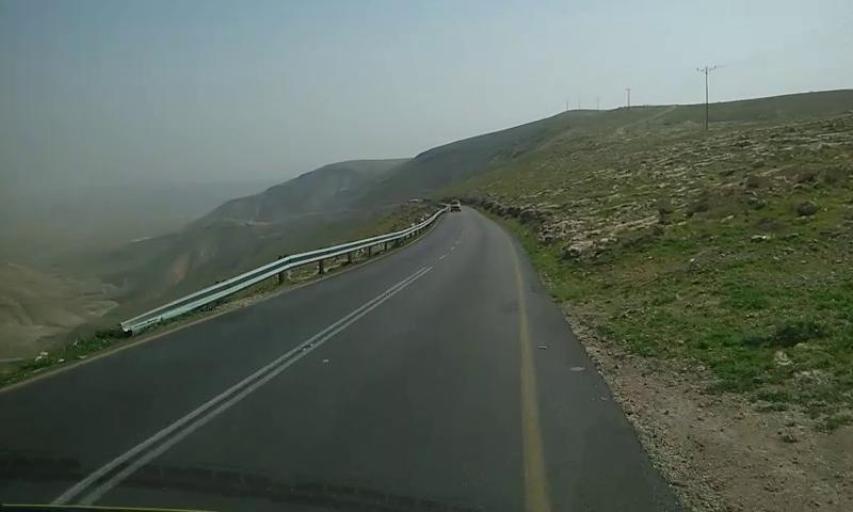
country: PS
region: West Bank
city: An Nuway`imah
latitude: 31.9105
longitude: 35.3667
